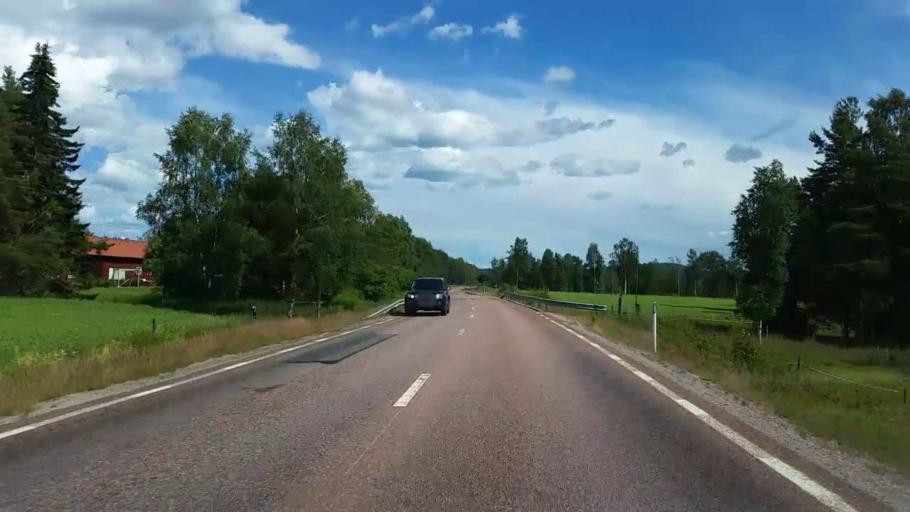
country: SE
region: Gaevleborg
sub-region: Ovanakers Kommun
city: Edsbyn
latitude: 61.3468
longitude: 15.6112
